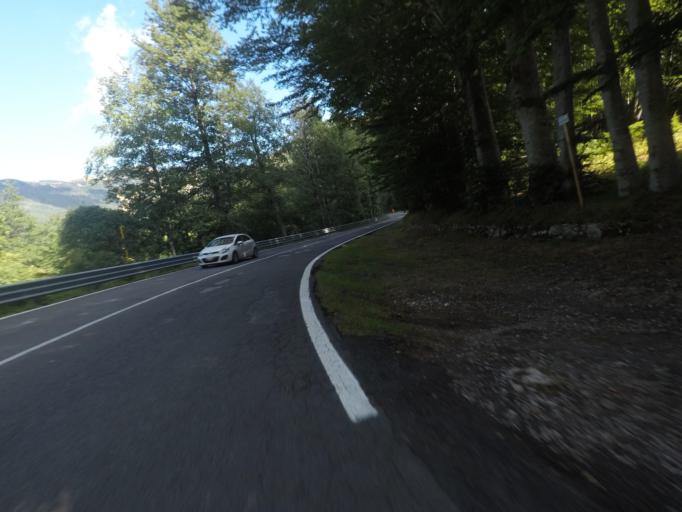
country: IT
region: Tuscany
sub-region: Provincia di Massa-Carrara
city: Comano
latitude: 44.2793
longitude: 10.1862
